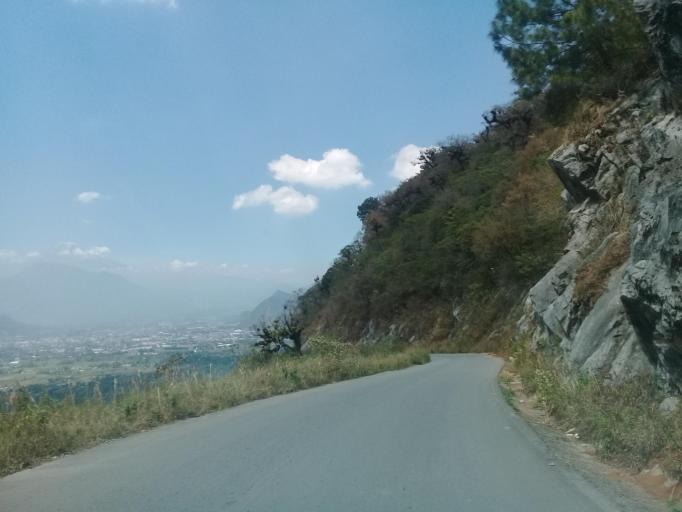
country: MX
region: Veracruz
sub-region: Tlilapan
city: Tonalixco
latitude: 18.8024
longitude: -97.0589
